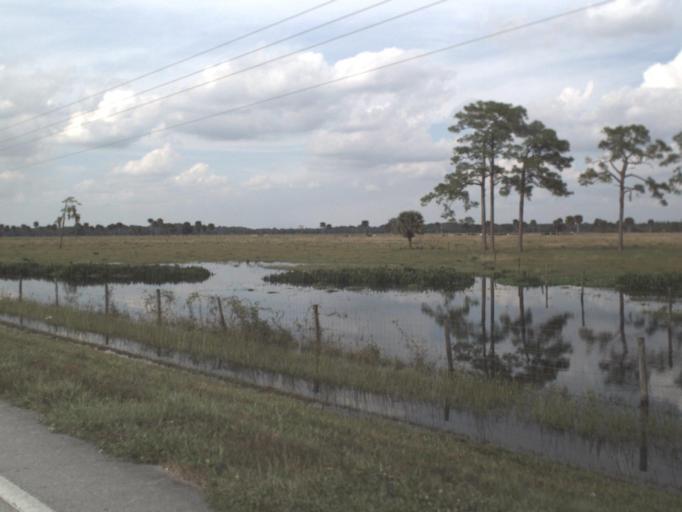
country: US
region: Florida
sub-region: Okeechobee County
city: Taylor Creek
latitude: 27.2241
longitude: -80.7678
